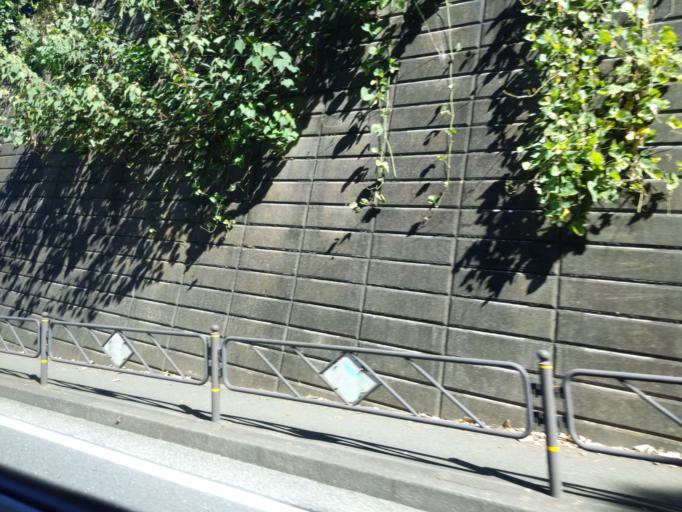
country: JP
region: Tokyo
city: Chofugaoka
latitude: 35.6509
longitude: 139.5866
